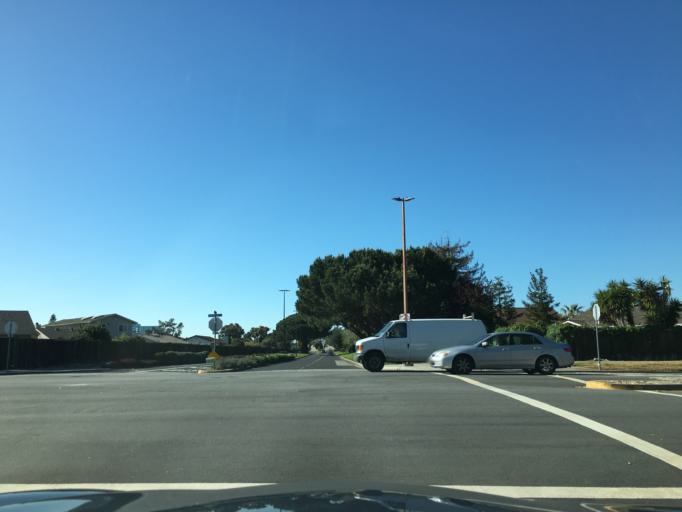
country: US
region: California
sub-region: San Mateo County
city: Redwood Shores
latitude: 37.5261
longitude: -122.2504
